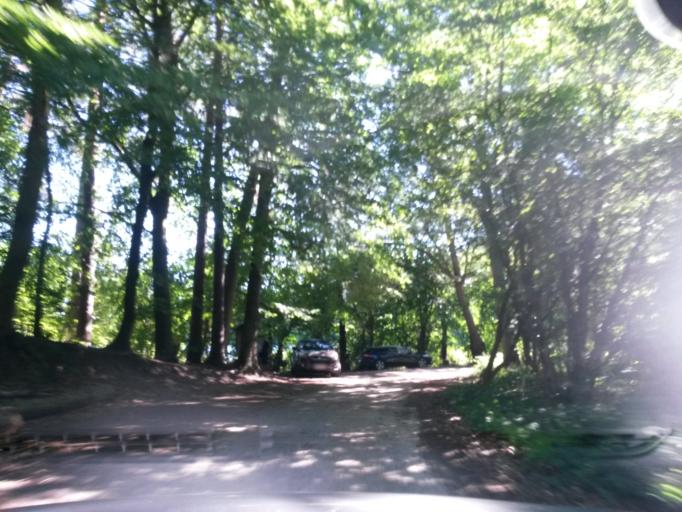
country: DE
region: Brandenburg
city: Lychen
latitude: 53.1836
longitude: 13.3523
